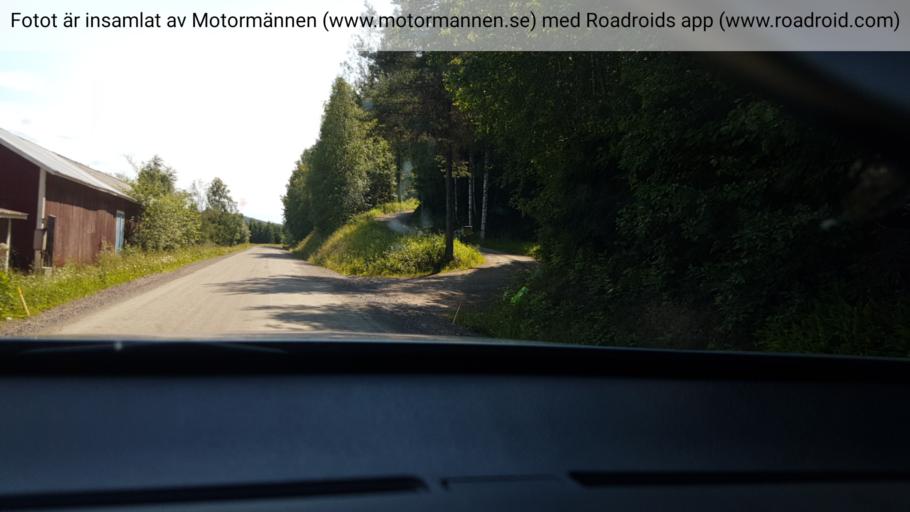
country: SE
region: Vaermland
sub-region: Hagfors Kommun
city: Ekshaerad
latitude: 60.4278
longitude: 13.2396
